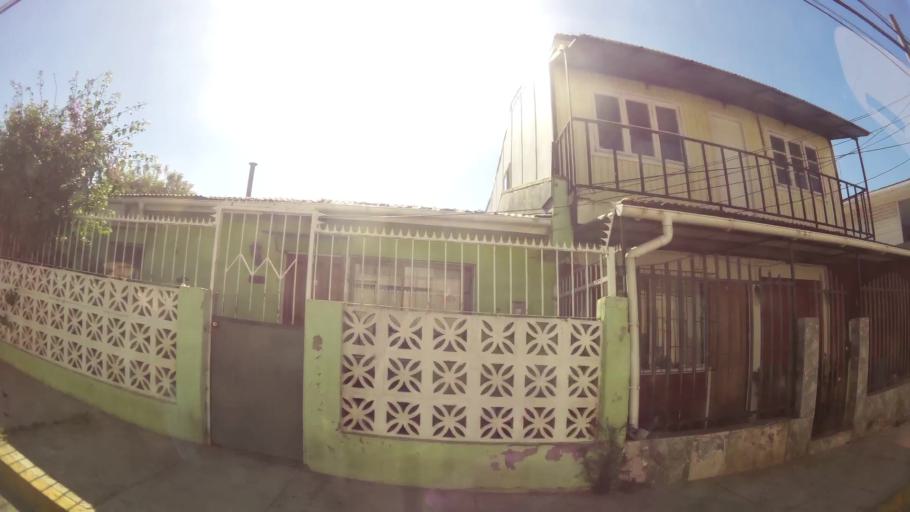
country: CL
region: Valparaiso
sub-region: Provincia de Valparaiso
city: Valparaiso
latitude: -33.0560
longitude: -71.6181
